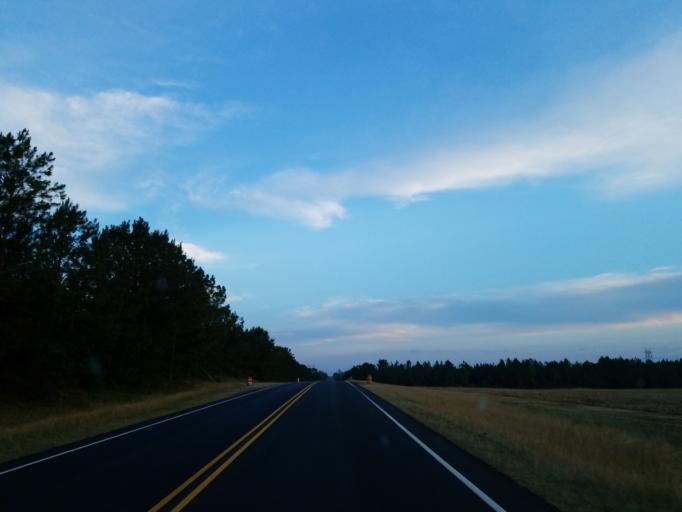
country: US
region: Georgia
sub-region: Turner County
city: Ashburn
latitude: 31.7177
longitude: -83.8081
